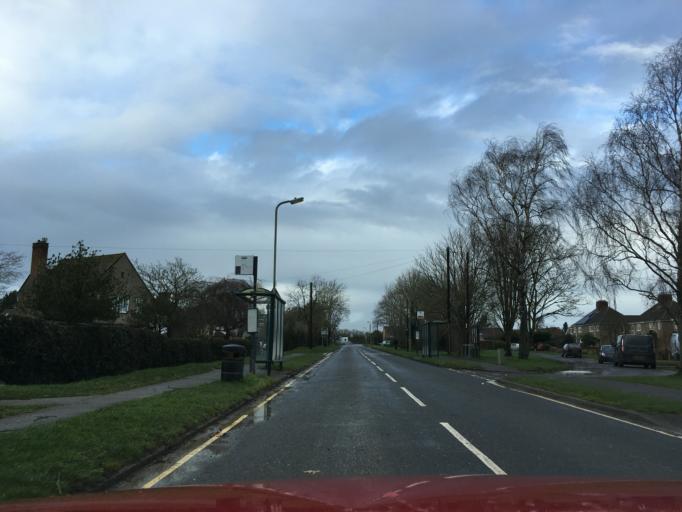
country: GB
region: England
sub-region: Oxfordshire
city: Eynsham
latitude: 51.7845
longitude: -1.3822
